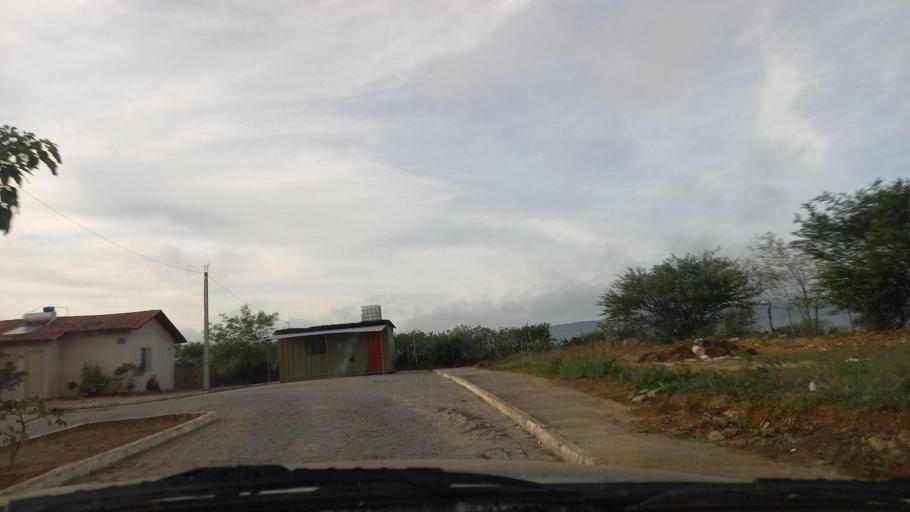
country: BR
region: Pernambuco
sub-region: Bezerros
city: Bezerros
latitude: -8.2180
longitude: -35.7393
